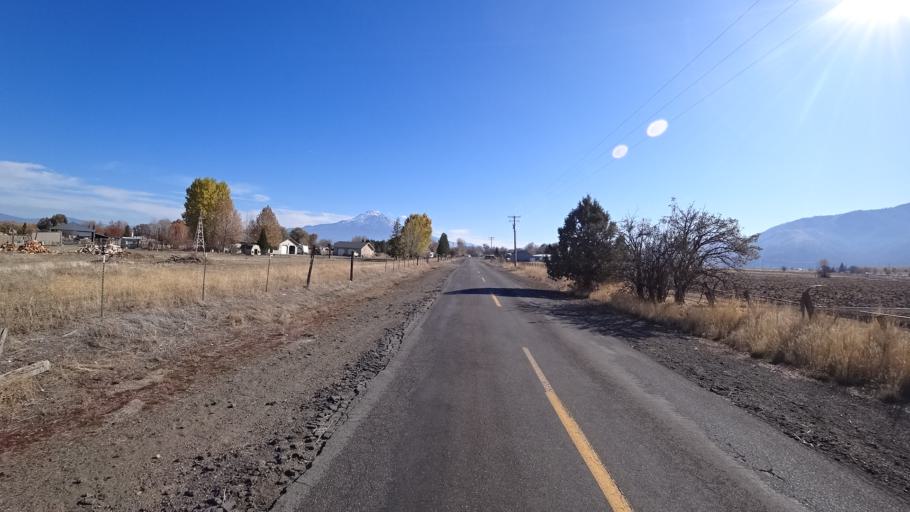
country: US
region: California
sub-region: Siskiyou County
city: Weed
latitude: 41.5221
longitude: -122.5253
